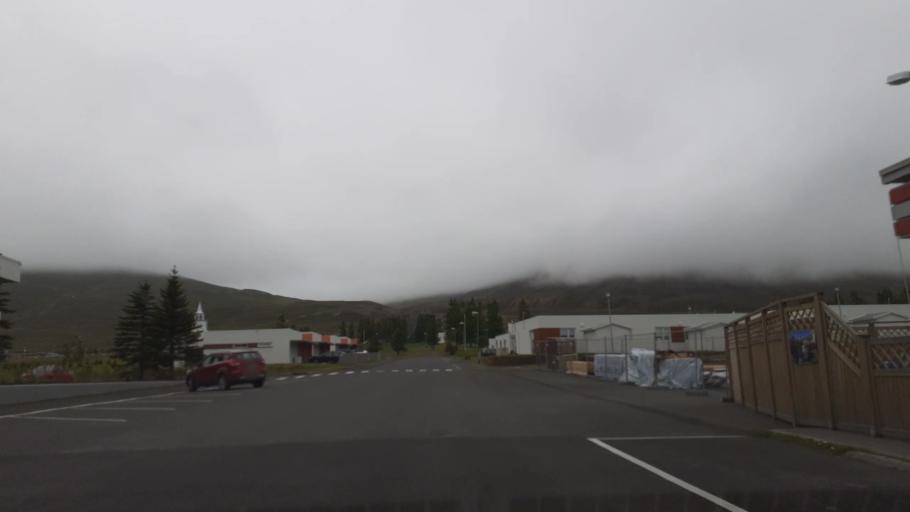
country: IS
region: Northeast
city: Dalvik
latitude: 65.9727
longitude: -18.5320
